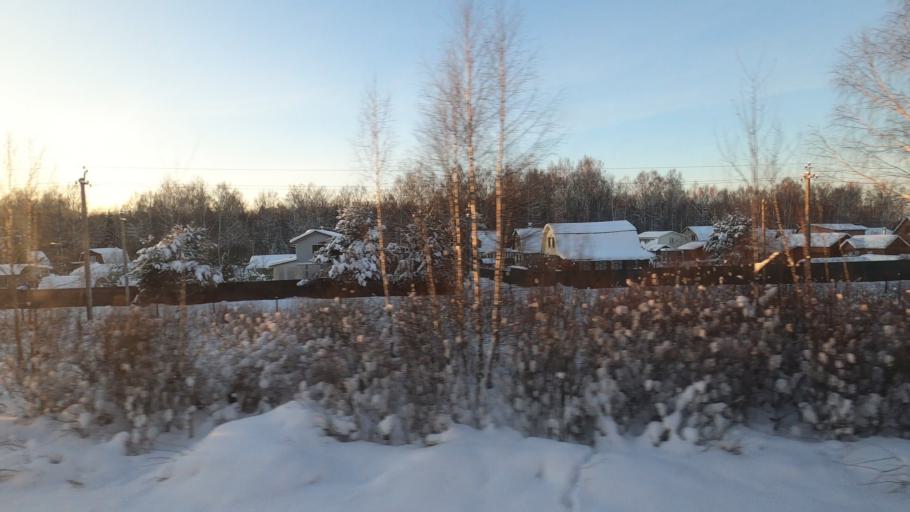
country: RU
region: Moskovskaya
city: Orud'yevo
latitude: 56.4320
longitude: 37.5013
